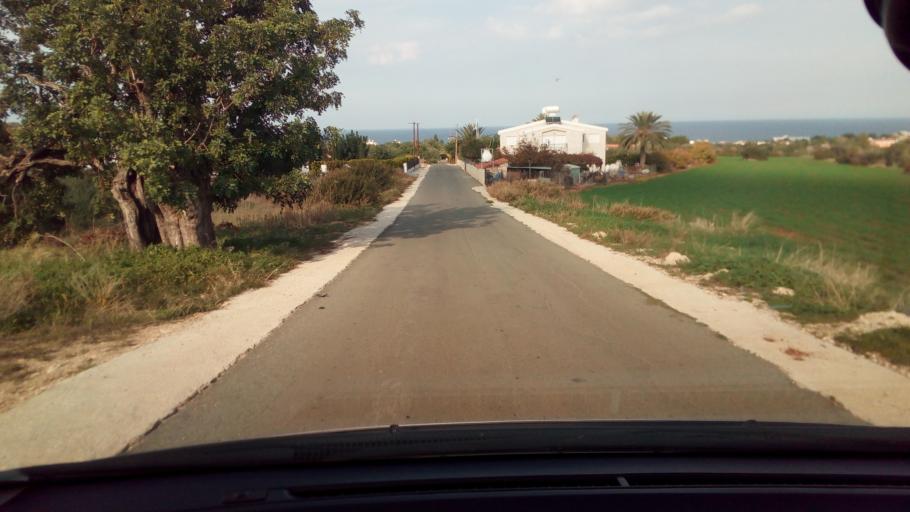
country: CY
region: Pafos
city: Polis
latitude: 35.0317
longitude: 32.3774
